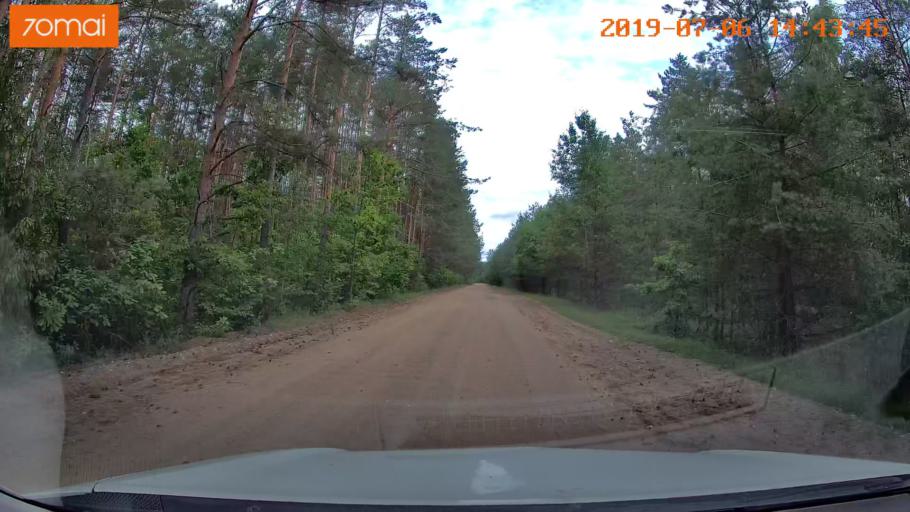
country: BY
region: Minsk
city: Ivyanyets
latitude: 53.9552
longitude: 26.6943
